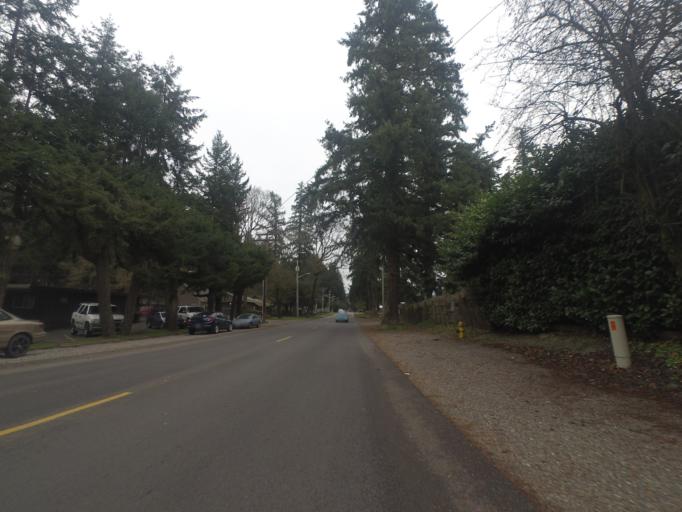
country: US
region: Washington
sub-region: Pierce County
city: McChord Air Force Base
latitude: 47.1212
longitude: -122.5247
